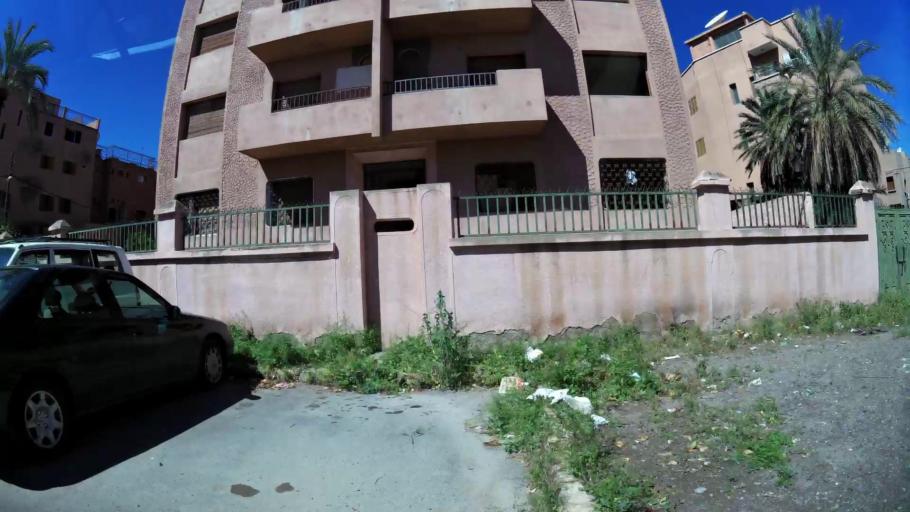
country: MA
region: Marrakech-Tensift-Al Haouz
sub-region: Marrakech
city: Marrakesh
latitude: 31.6422
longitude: -8.0079
